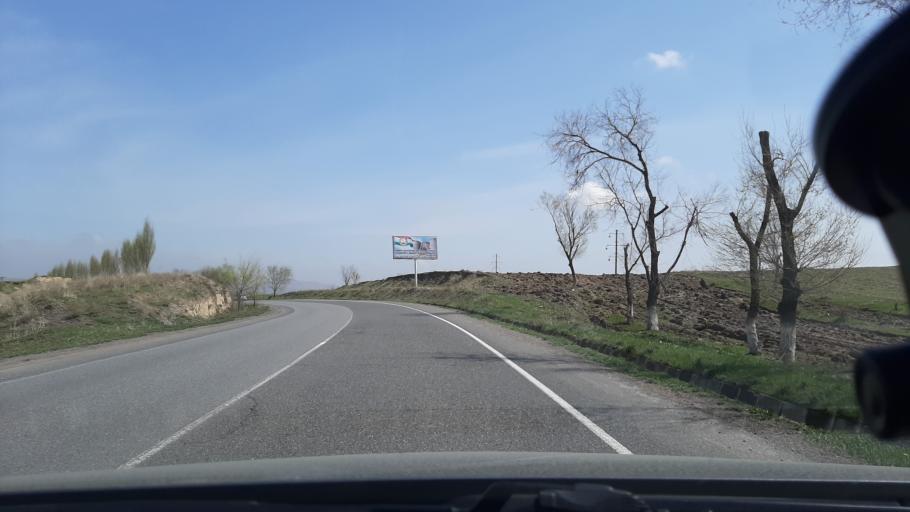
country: TJ
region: Viloyati Sughd
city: Shahriston
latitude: 39.7921
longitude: 68.8772
